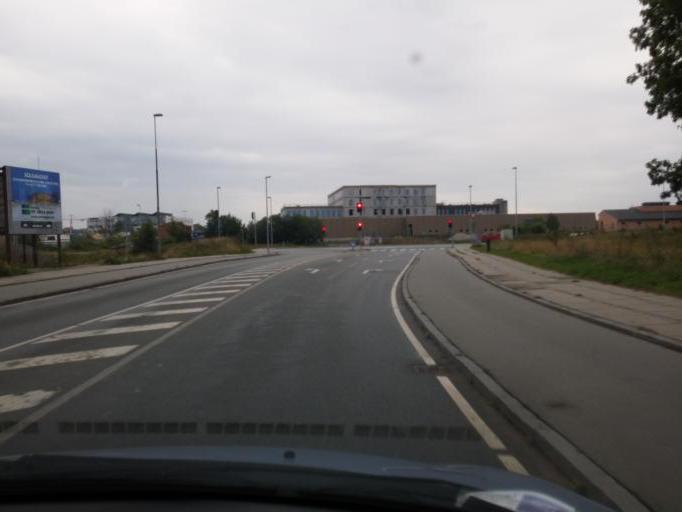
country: DK
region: South Denmark
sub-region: Odense Kommune
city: Odense
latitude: 55.4061
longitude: 10.3772
